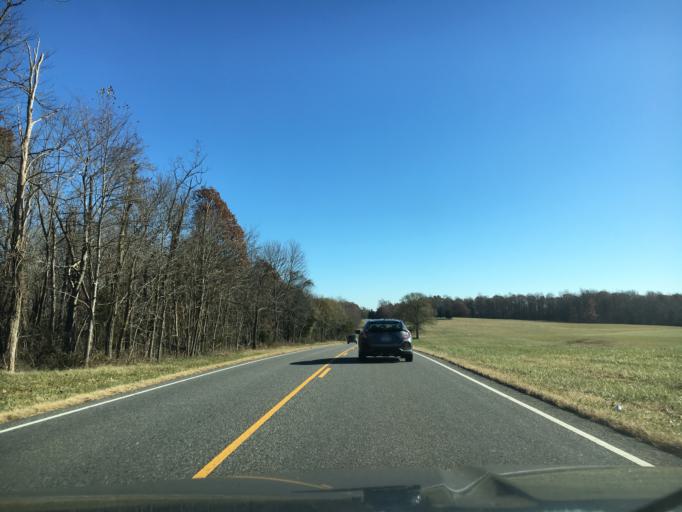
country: US
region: Virginia
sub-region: Appomattox County
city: Appomattox
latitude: 37.3737
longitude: -78.8159
